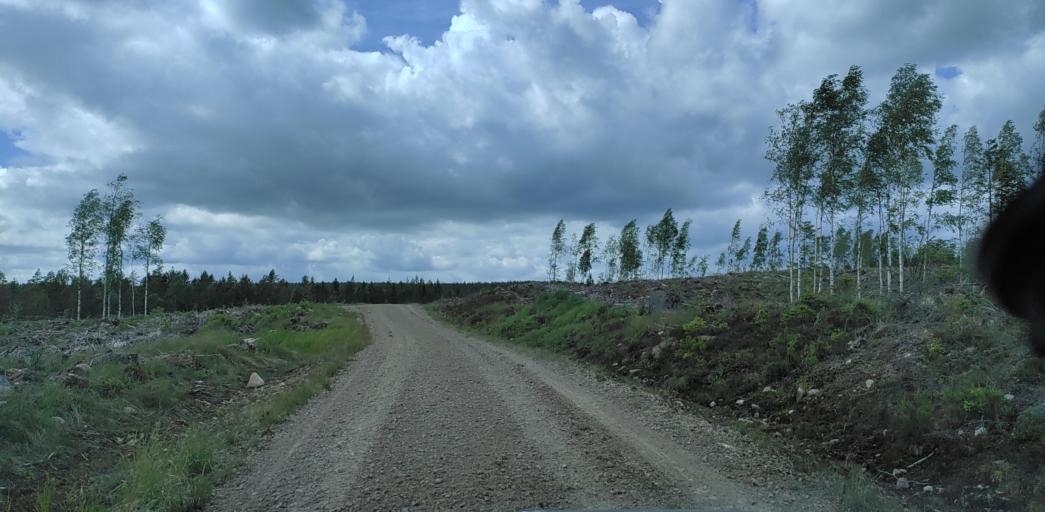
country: SE
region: Vaermland
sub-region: Munkfors Kommun
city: Munkfors
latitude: 59.9493
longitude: 13.4179
